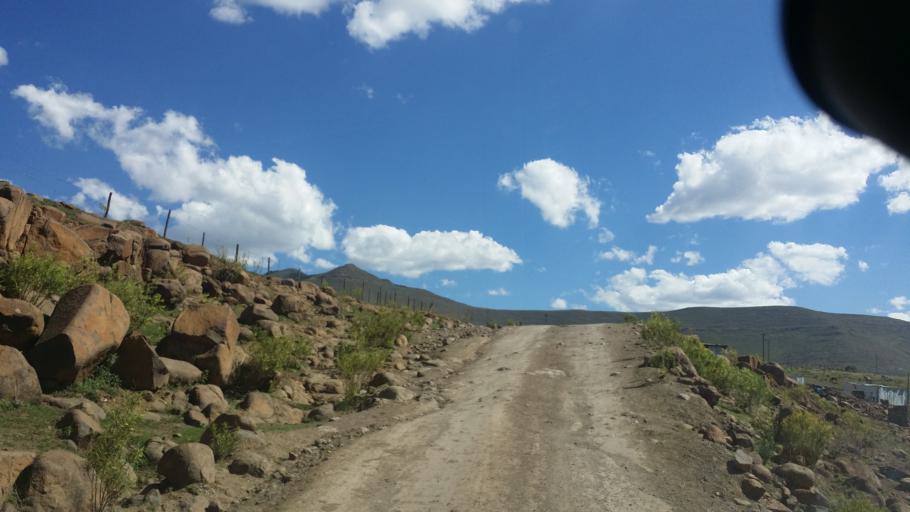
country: LS
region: Mokhotlong
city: Mokhotlong
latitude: -29.2755
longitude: 29.0678
